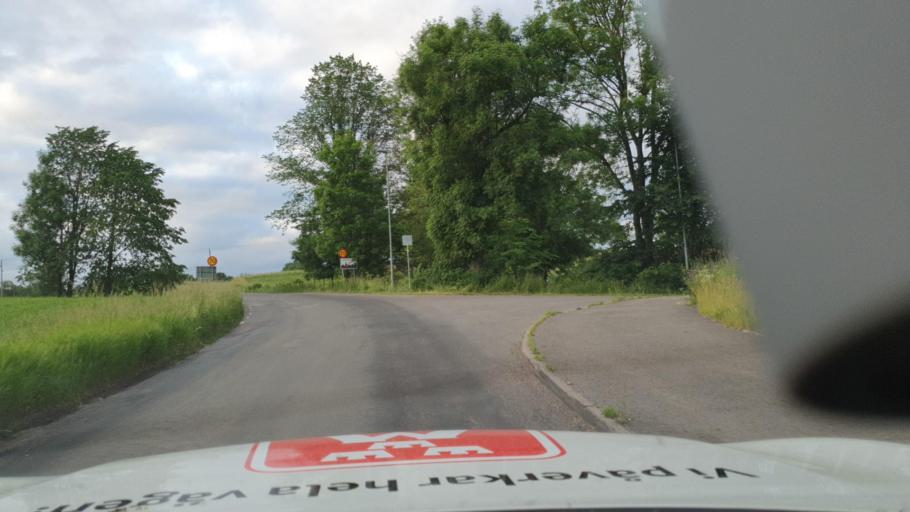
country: SE
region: Vaestra Goetaland
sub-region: Falkopings Kommun
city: Akarp
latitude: 58.2129
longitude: 13.6014
